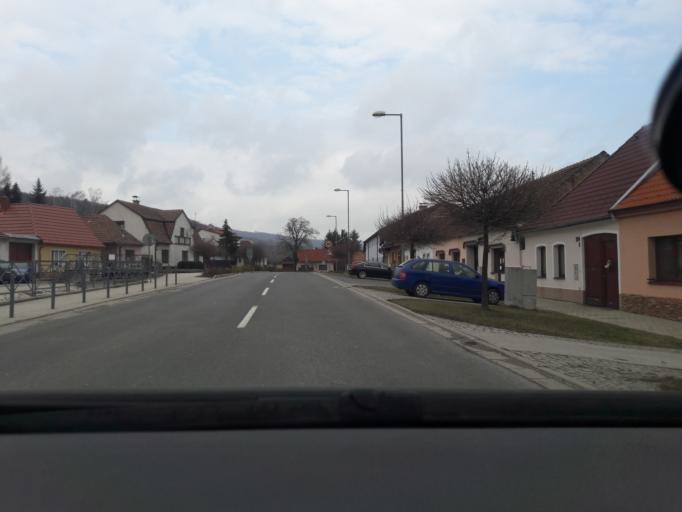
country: SK
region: Bratislavsky
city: Modra
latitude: 48.4010
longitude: 17.3585
